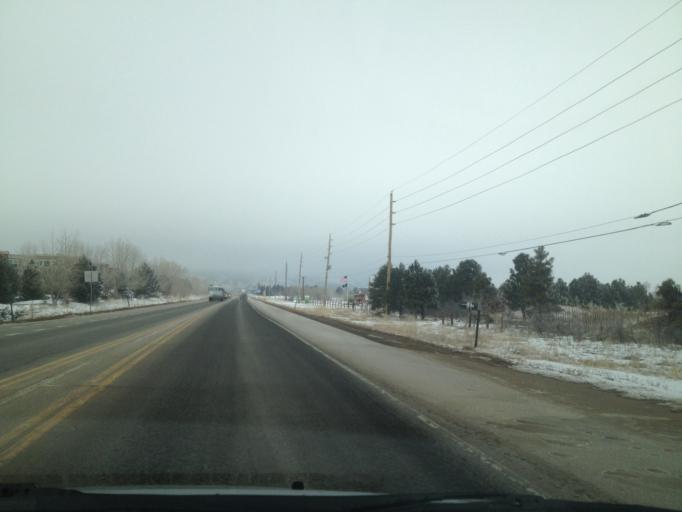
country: US
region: Colorado
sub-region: Boulder County
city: Boulder
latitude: 40.0590
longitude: -105.2720
